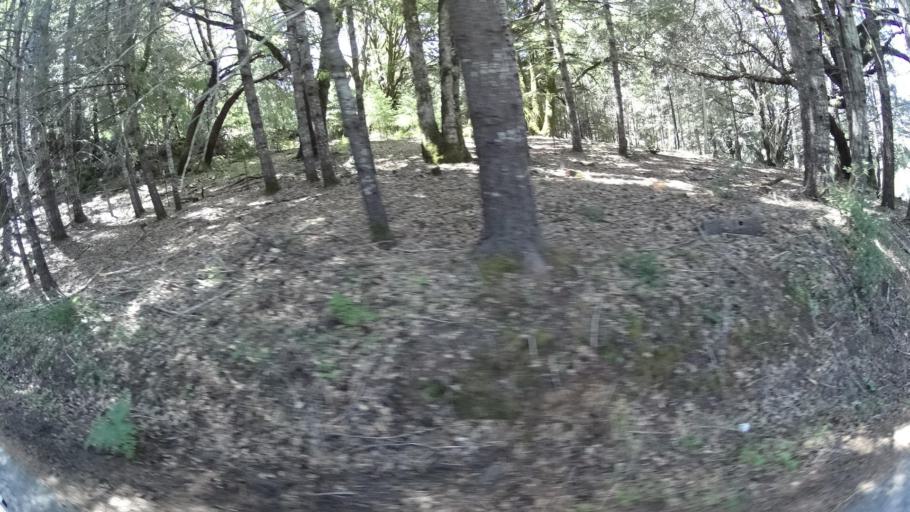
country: US
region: California
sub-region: Humboldt County
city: Redway
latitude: 40.1356
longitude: -123.9825
